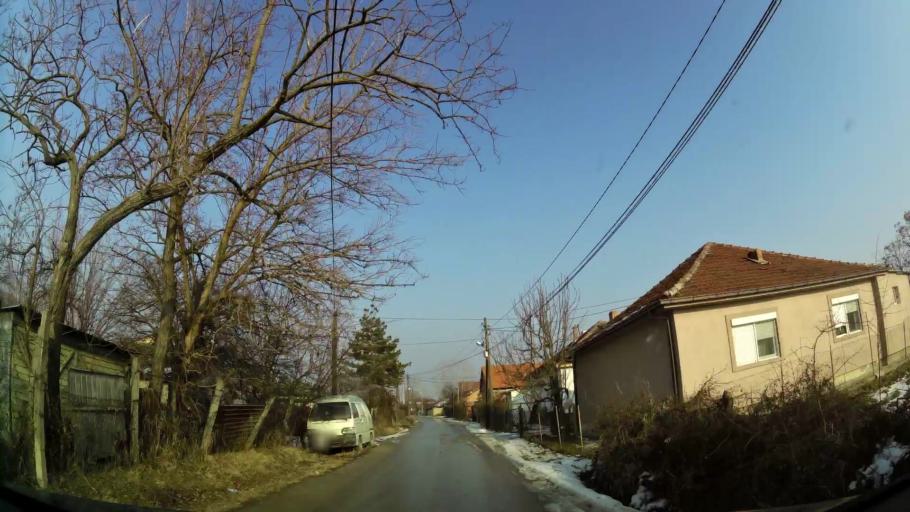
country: MK
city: Kadino
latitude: 41.9661
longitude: 21.5942
